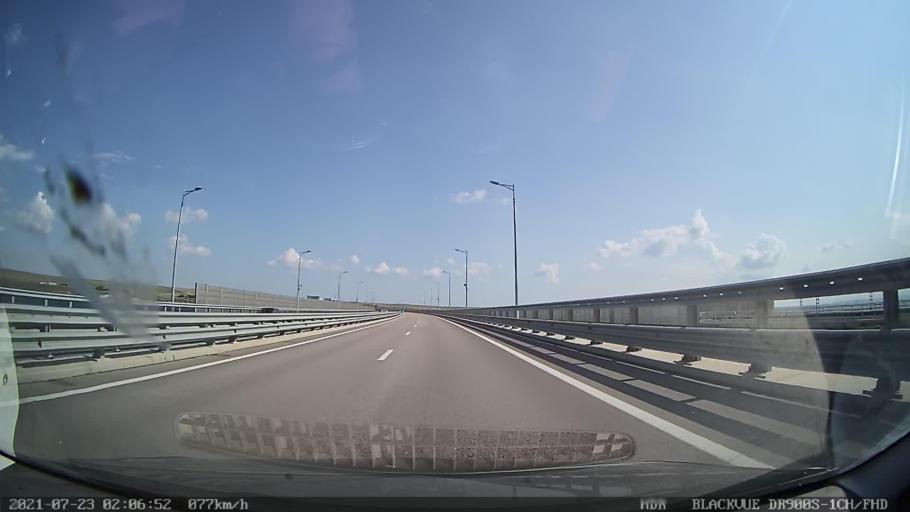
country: RU
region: Krasnodarskiy
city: Taman'
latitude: 45.2139
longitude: 36.6082
